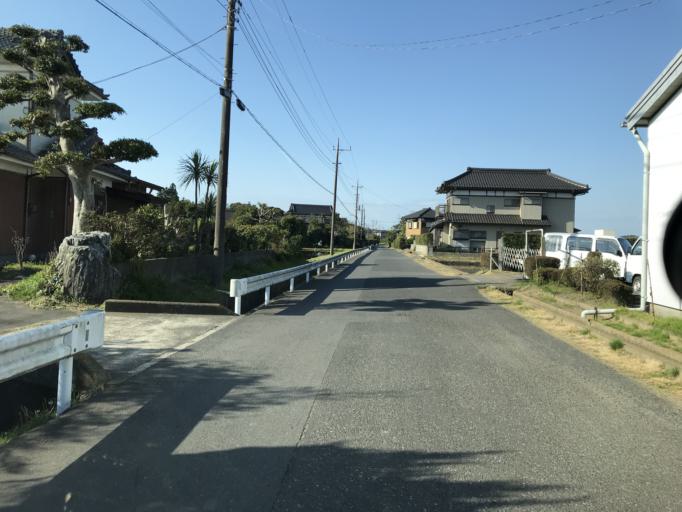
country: JP
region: Chiba
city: Omigawa
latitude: 35.8423
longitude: 140.6016
